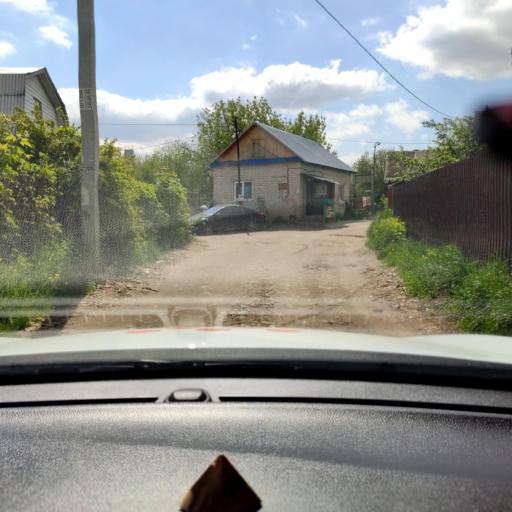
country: RU
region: Tatarstan
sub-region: Gorod Kazan'
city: Kazan
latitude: 55.8594
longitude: 49.1905
